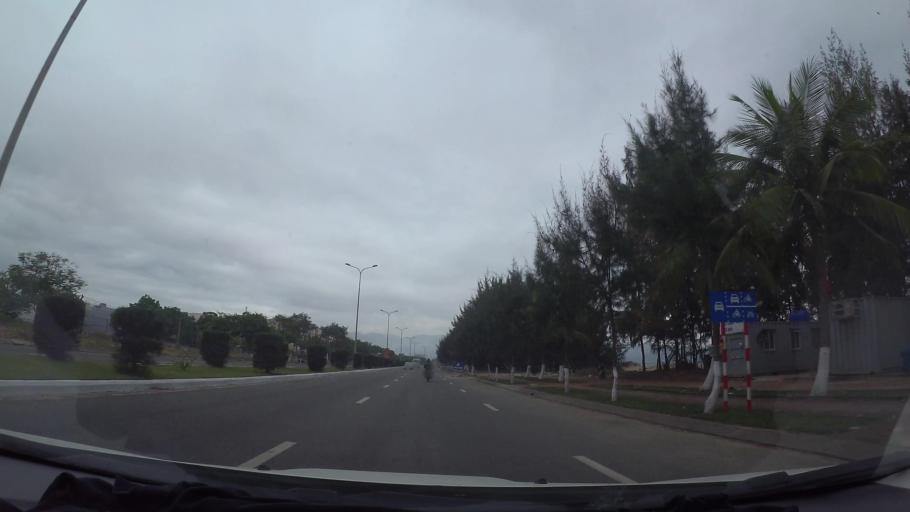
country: VN
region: Da Nang
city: Lien Chieu
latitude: 16.1058
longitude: 108.1360
